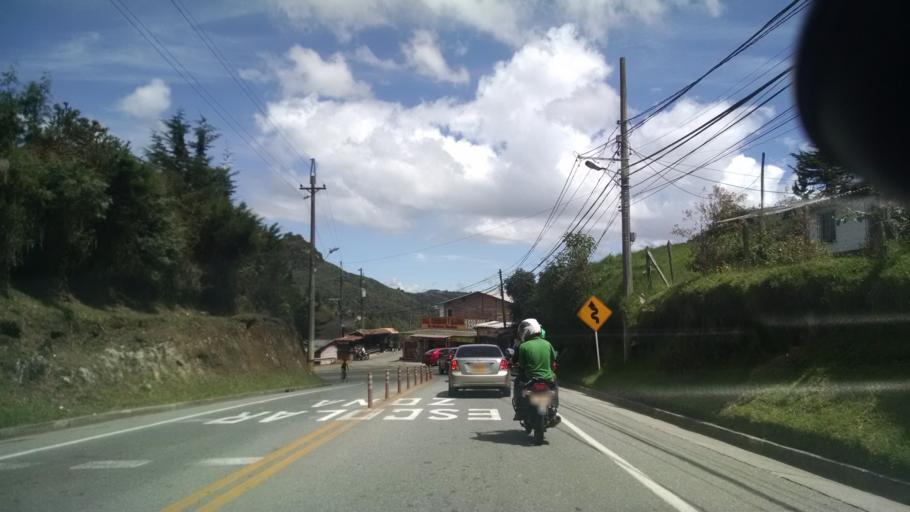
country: CO
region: Antioquia
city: Envigado
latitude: 6.1398
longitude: -75.5205
